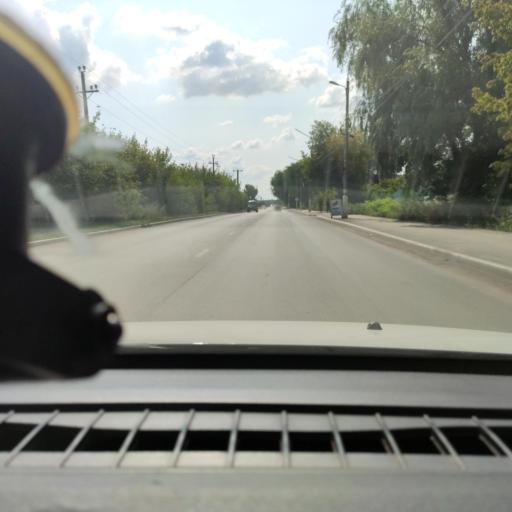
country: RU
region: Samara
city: Chapayevsk
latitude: 52.9814
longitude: 49.7056
